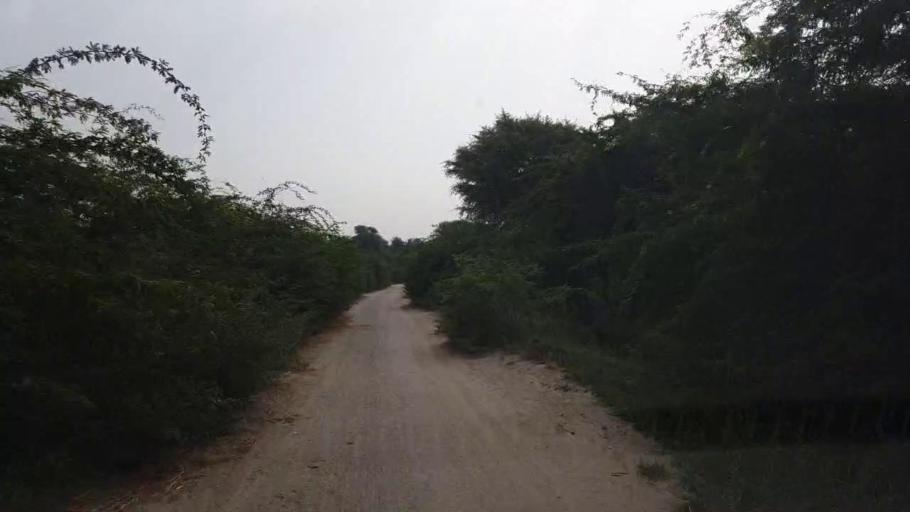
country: PK
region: Sindh
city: Matli
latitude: 24.9974
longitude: 68.7027
